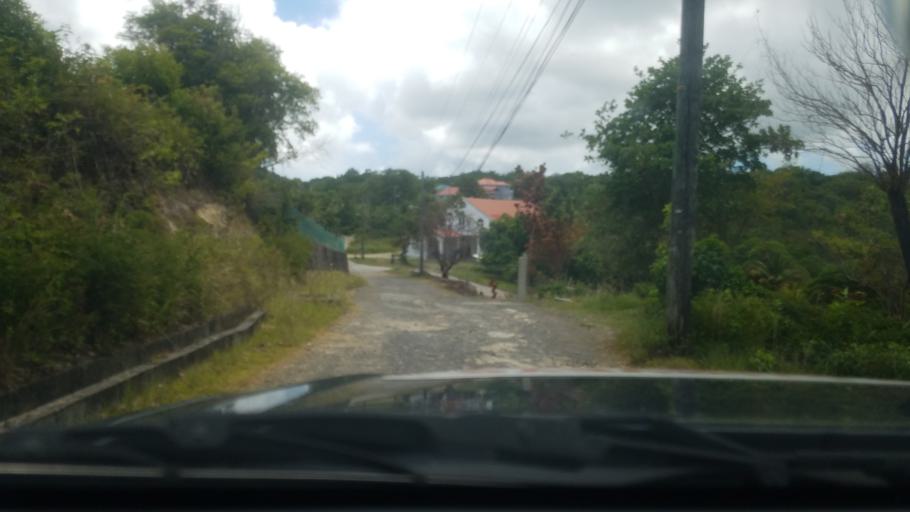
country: LC
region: Dennery Quarter
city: Dennery
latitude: 13.9194
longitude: -60.8989
